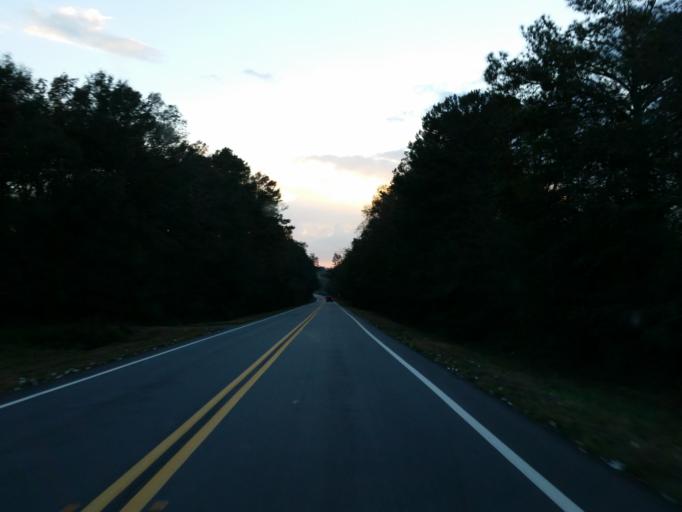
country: US
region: Georgia
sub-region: Pulaski County
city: Hawkinsville
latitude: 32.2227
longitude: -83.5222
